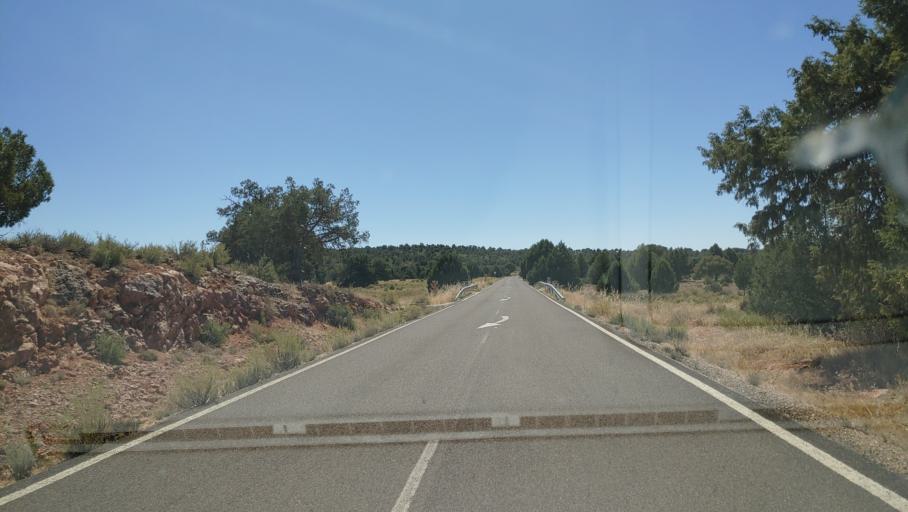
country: ES
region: Castille-La Mancha
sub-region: Provincia de Albacete
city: Ossa de Montiel
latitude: 38.8732
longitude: -2.7868
